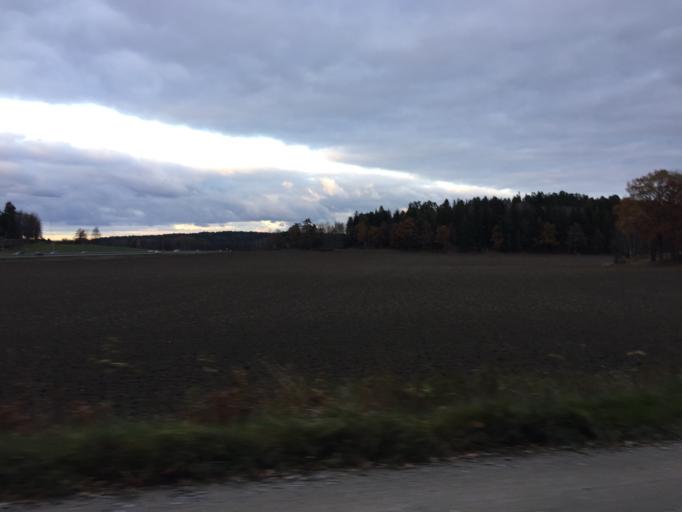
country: SE
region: Stockholm
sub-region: Botkyrka Kommun
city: Eriksberg
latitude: 59.2240
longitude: 17.7891
